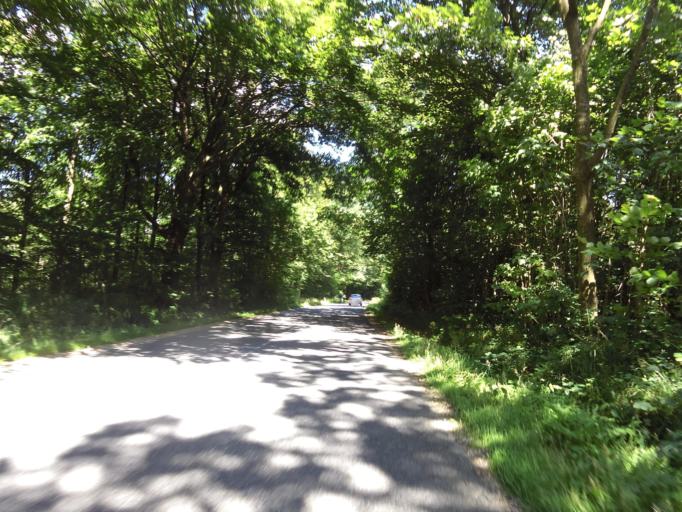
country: DK
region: South Denmark
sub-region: Haderslev Kommune
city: Gram
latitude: 55.3051
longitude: 9.0689
